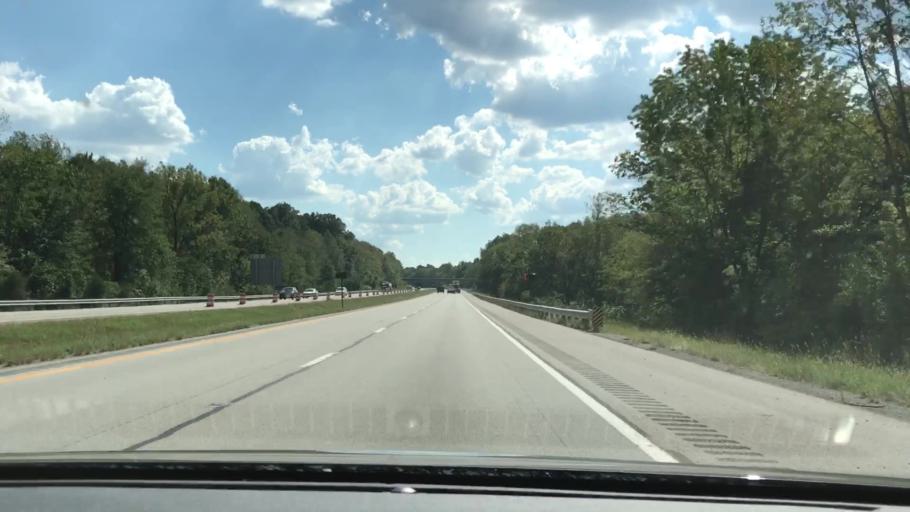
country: US
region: Kentucky
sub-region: Ohio County
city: Oak Grove
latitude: 37.2725
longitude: -86.7466
